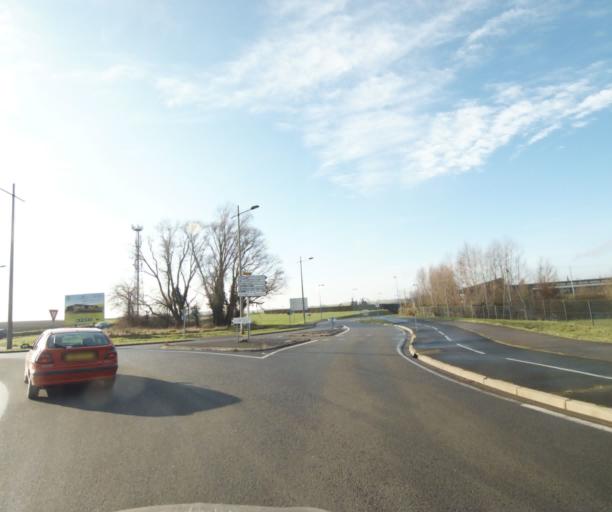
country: FR
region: Nord-Pas-de-Calais
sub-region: Departement du Nord
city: Thiant
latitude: 50.3043
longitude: 3.4618
